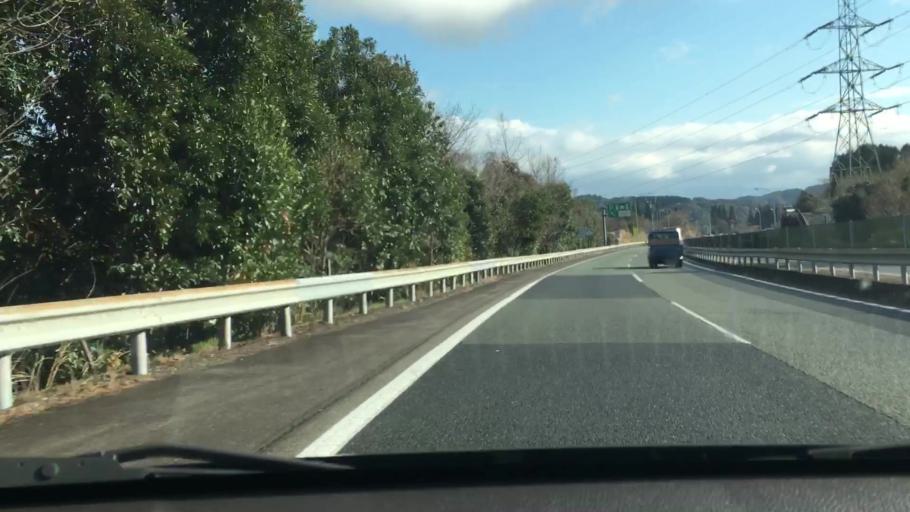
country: JP
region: Kumamoto
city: Hitoyoshi
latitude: 32.2652
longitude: 130.7660
